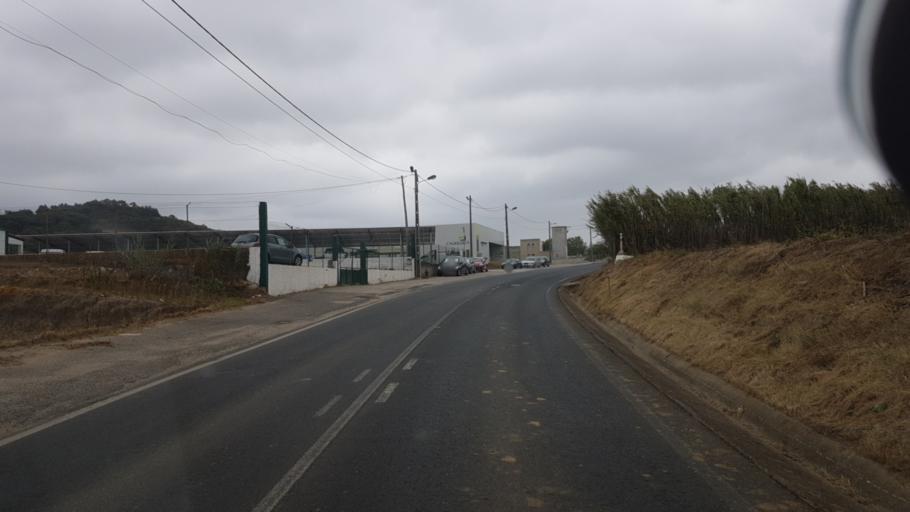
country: PT
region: Lisbon
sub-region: Lourinha
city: Lourinha
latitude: 39.2294
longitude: -9.3118
